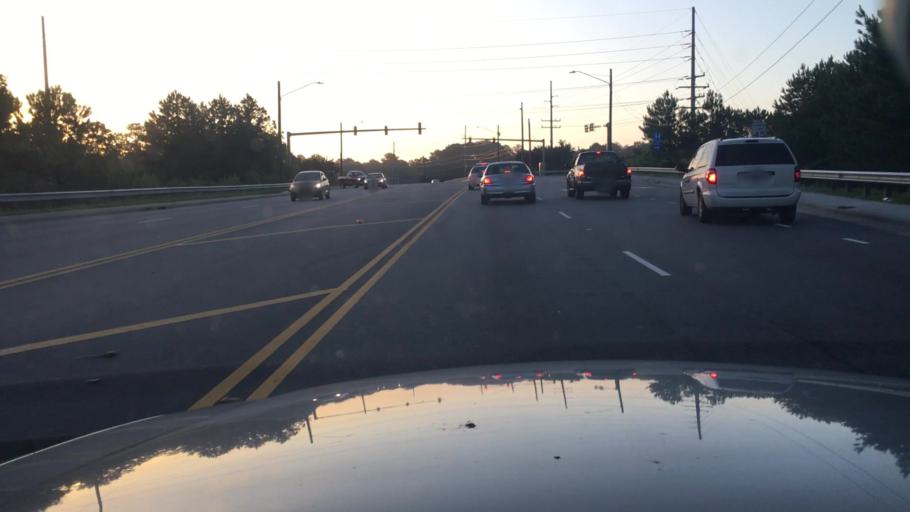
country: US
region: North Carolina
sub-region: Cumberland County
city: Fayetteville
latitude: 35.0594
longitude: -78.9559
